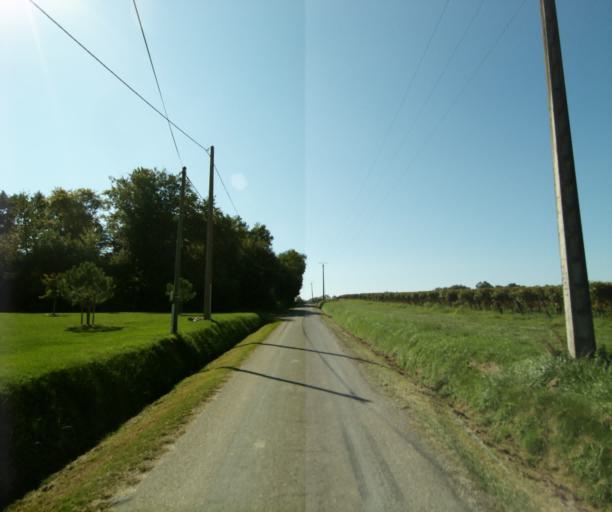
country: FR
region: Midi-Pyrenees
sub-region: Departement du Gers
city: Cazaubon
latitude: 43.9247
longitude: -0.0261
